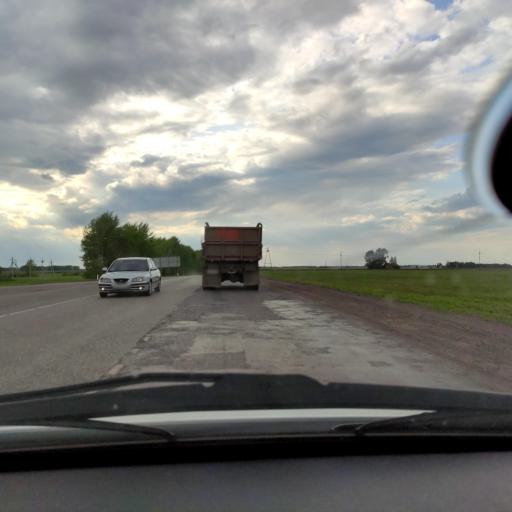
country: RU
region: Bashkortostan
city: Dyurtyuli
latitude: 55.3803
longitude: 54.8648
